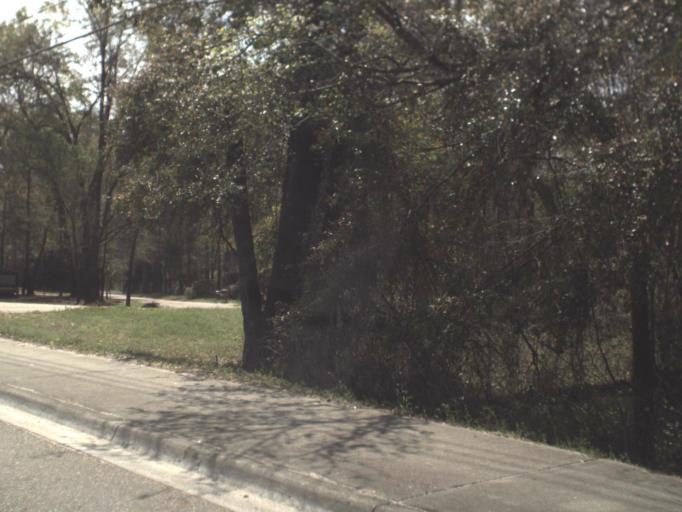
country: US
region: Florida
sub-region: Leon County
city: Tallahassee
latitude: 30.4657
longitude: -84.2297
